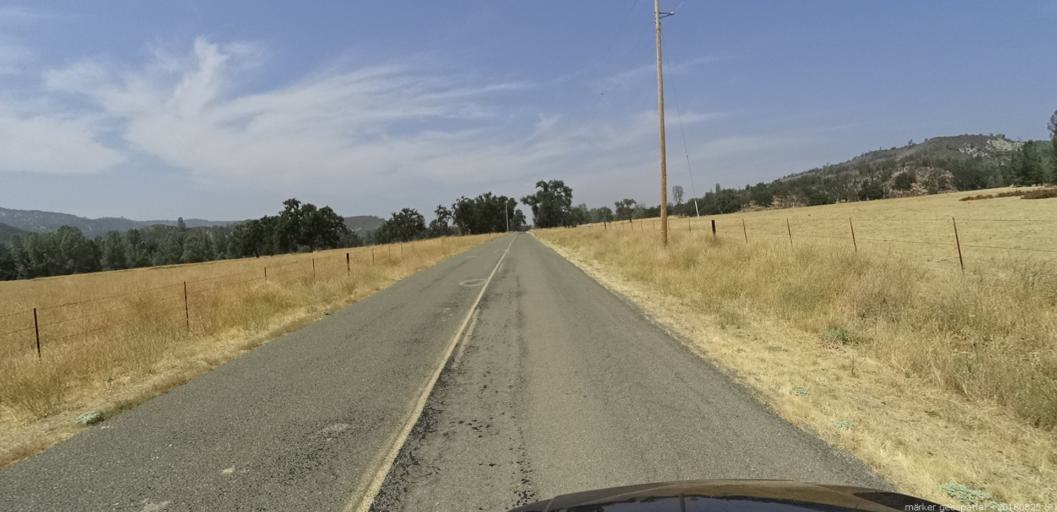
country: US
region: California
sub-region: Fresno County
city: Coalinga
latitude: 35.9143
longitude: -120.4826
